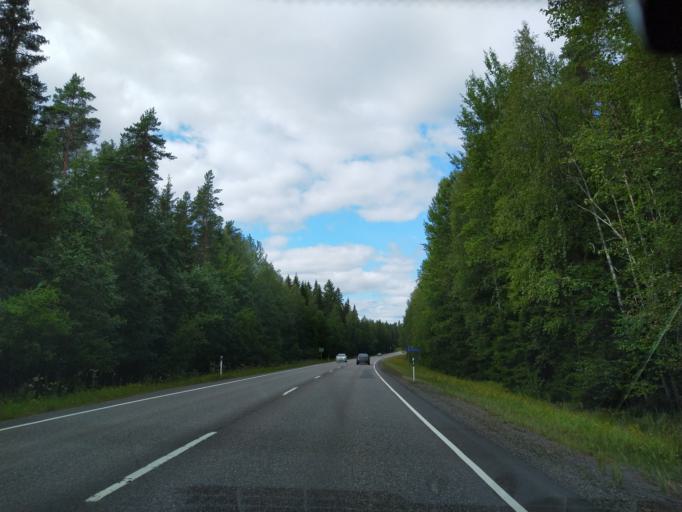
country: FI
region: Haeme
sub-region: Riihimaeki
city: Loppi
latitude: 60.7491
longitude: 24.3214
